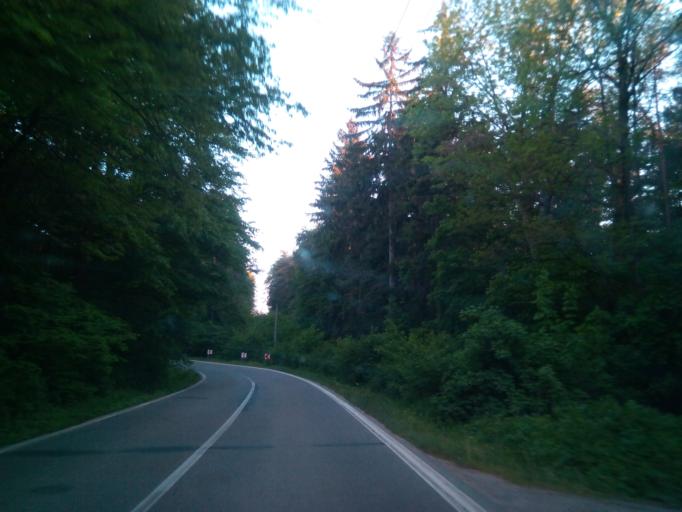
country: CZ
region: South Moravian
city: Bilovice nad Svitavou
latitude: 49.2403
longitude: 16.7118
